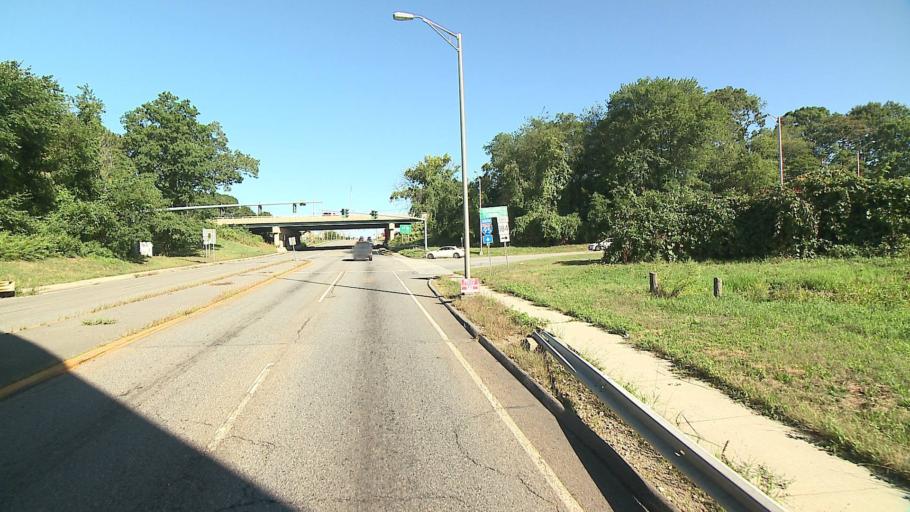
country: US
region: Connecticut
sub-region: New London County
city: Groton
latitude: 41.3650
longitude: -72.0679
